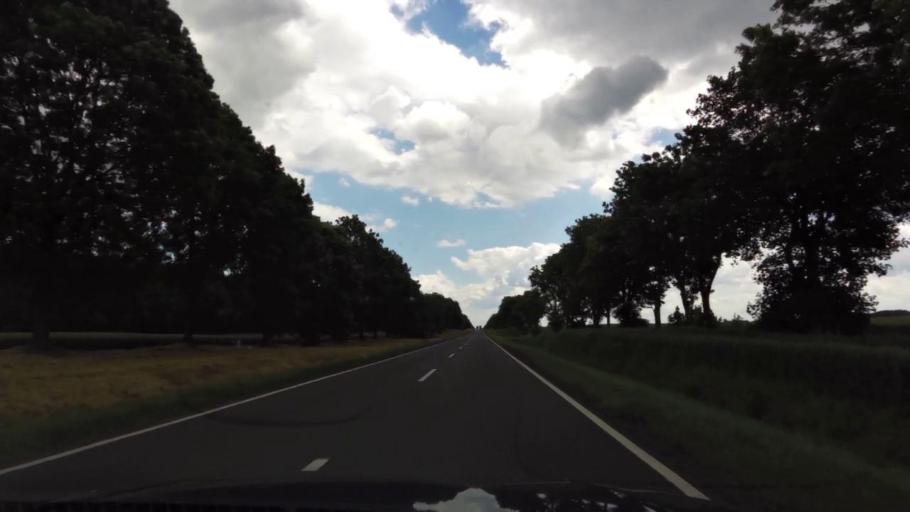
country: PL
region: West Pomeranian Voivodeship
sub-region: Powiat mysliborski
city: Mysliborz
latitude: 52.9658
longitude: 14.7481
